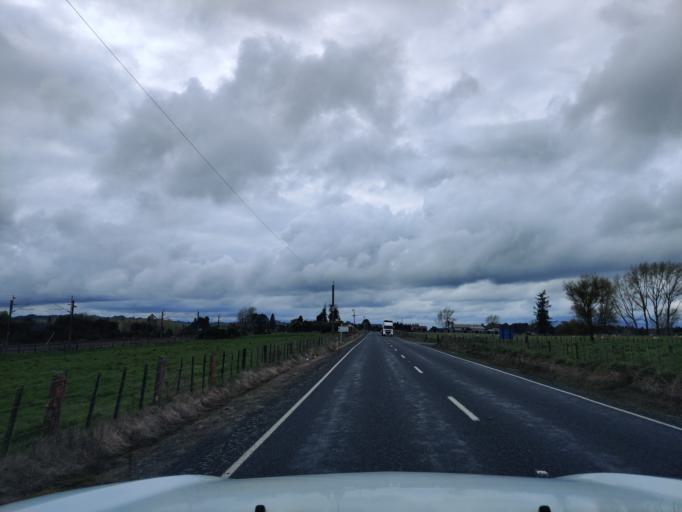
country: NZ
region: Waikato
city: Turangi
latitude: -39.0093
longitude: 175.3776
